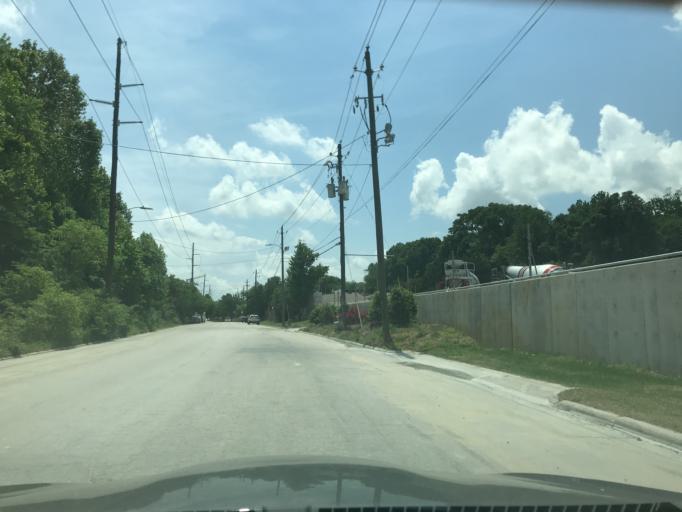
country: US
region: North Carolina
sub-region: Wake County
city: West Raleigh
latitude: 35.7956
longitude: -78.6421
